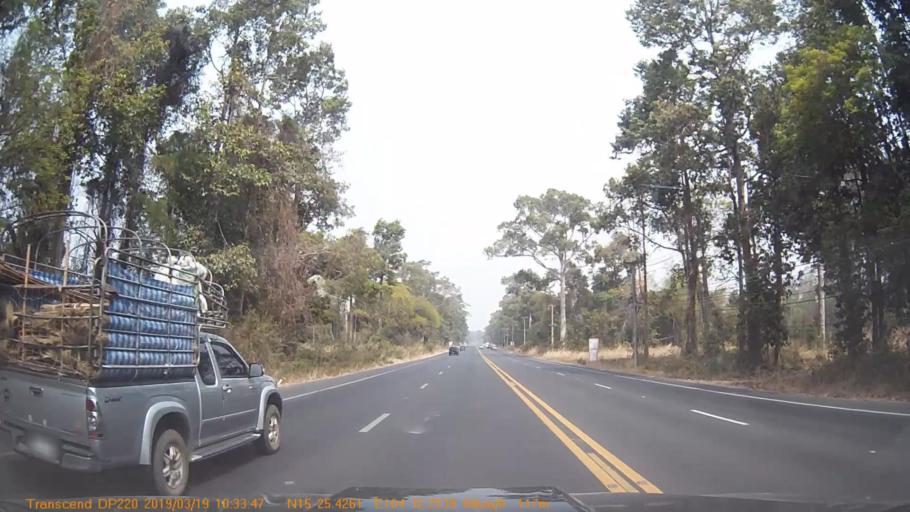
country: TH
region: Changwat Ubon Ratchathani
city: Khueang Nai
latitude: 15.4241
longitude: 104.5374
